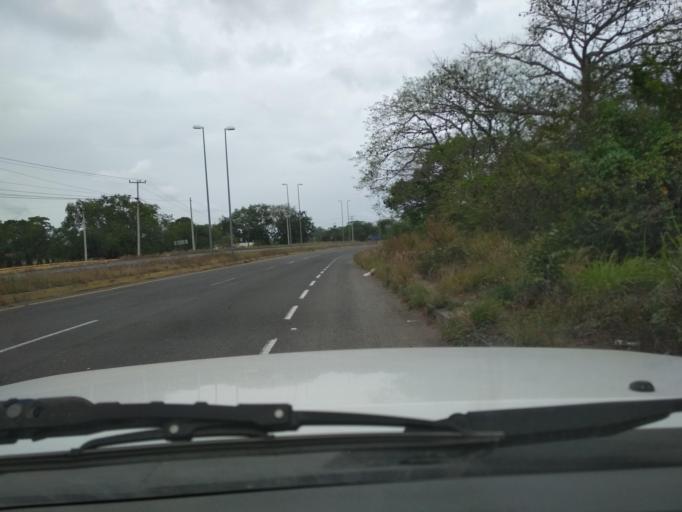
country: MX
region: Veracruz
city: El Tejar
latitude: 19.0672
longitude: -96.1311
